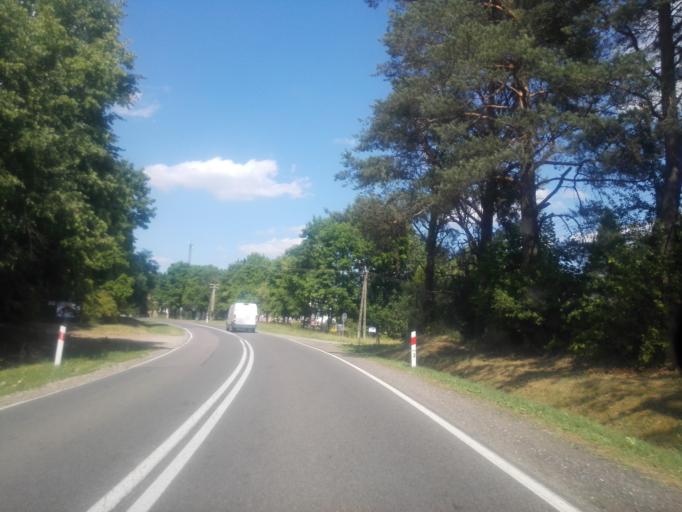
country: PL
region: Podlasie
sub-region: Powiat sejnenski
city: Sejny
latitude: 53.9800
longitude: 23.2923
